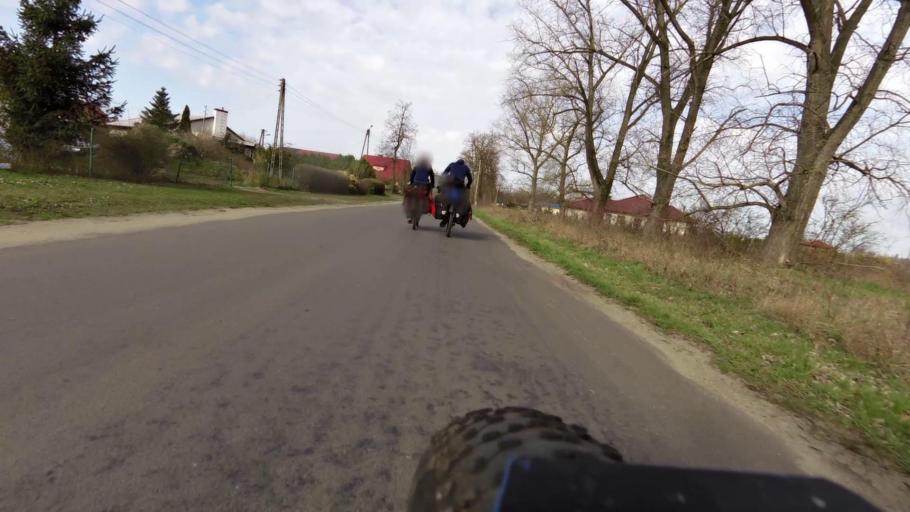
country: DE
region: Brandenburg
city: Brieskow-Finkenheerd
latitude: 52.3028
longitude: 14.5951
